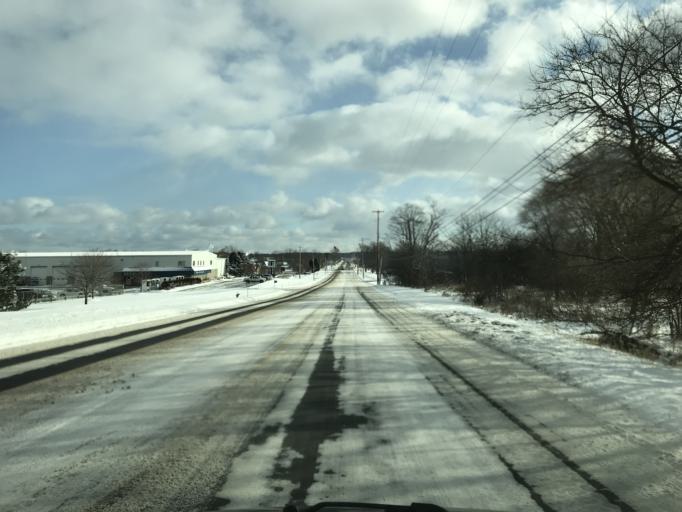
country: US
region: Michigan
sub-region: Kent County
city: Cutlerville
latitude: 42.8264
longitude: -85.6892
